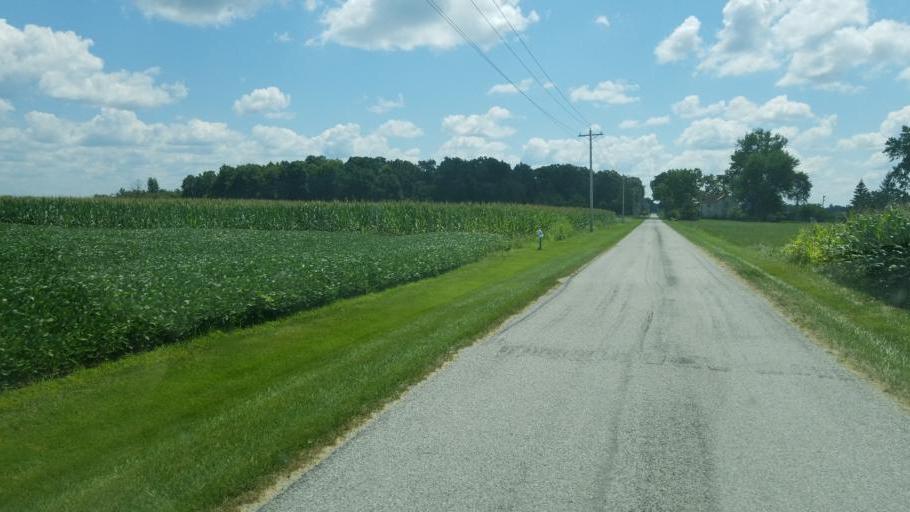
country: US
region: Ohio
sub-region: Marion County
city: Marion
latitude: 40.6669
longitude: -83.0923
